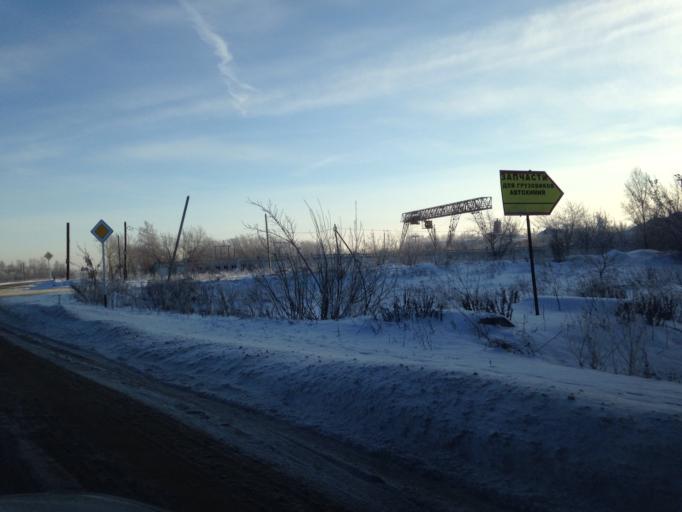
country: RU
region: Ulyanovsk
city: Novoul'yanovsk
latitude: 54.1628
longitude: 48.3621
